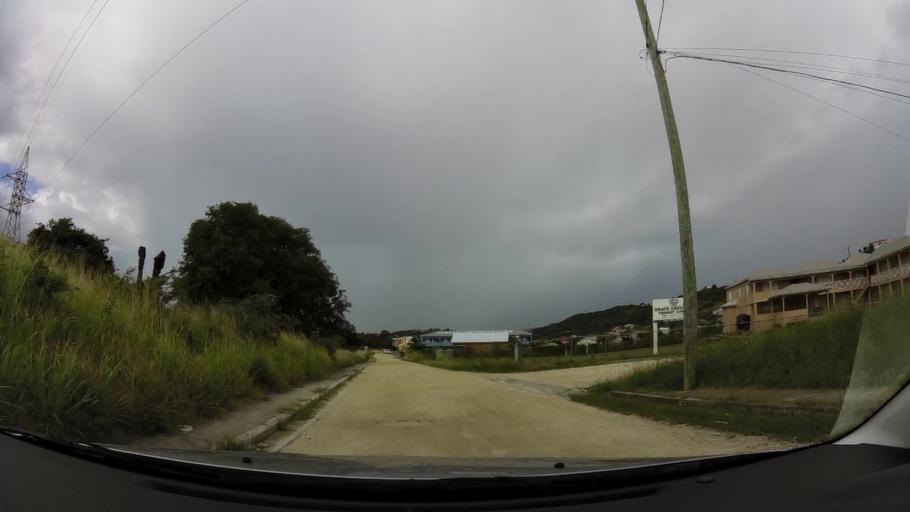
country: AG
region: Saint John
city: Potters Village
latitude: 17.0982
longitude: -61.8248
